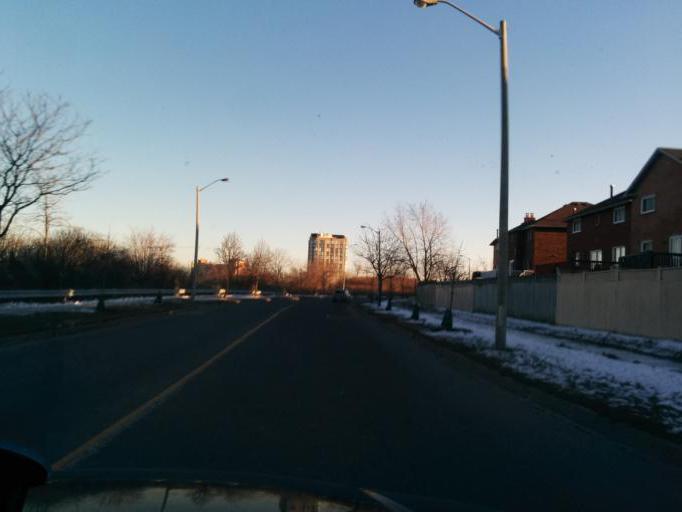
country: CA
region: Ontario
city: Etobicoke
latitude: 43.7235
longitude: -79.6142
